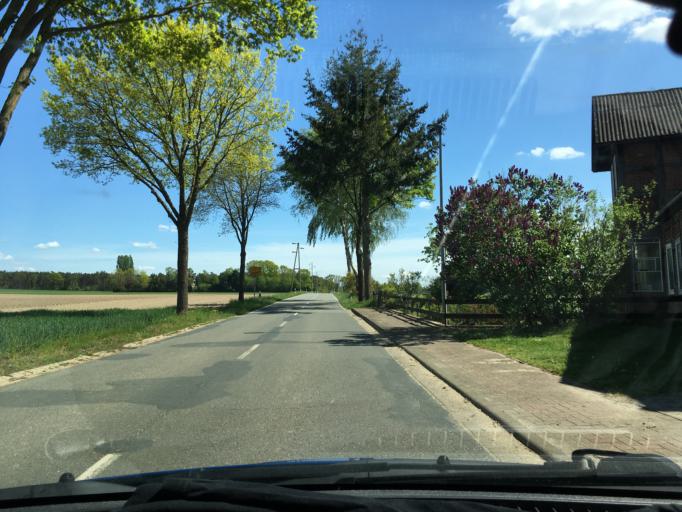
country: DE
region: Lower Saxony
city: Zernien
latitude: 53.0246
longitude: 10.8860
